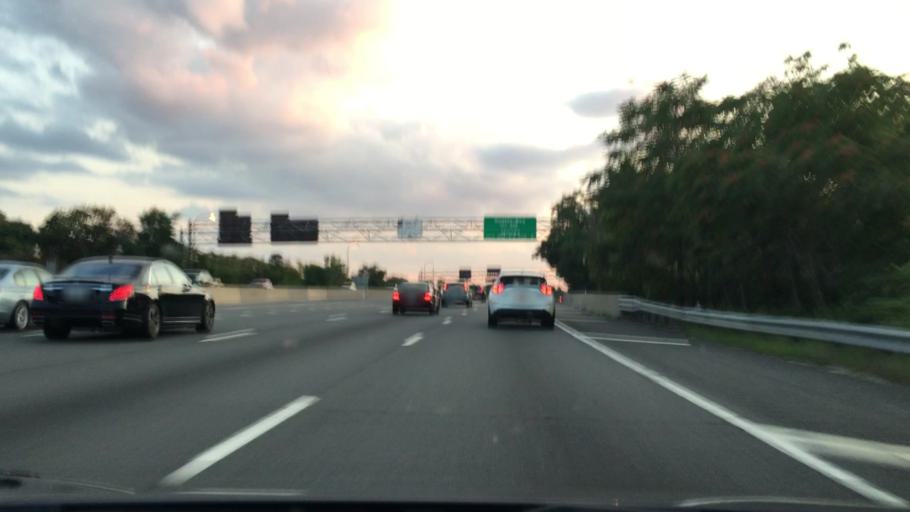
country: US
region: New York
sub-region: Nassau County
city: Jericho
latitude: 40.7883
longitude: -73.5259
